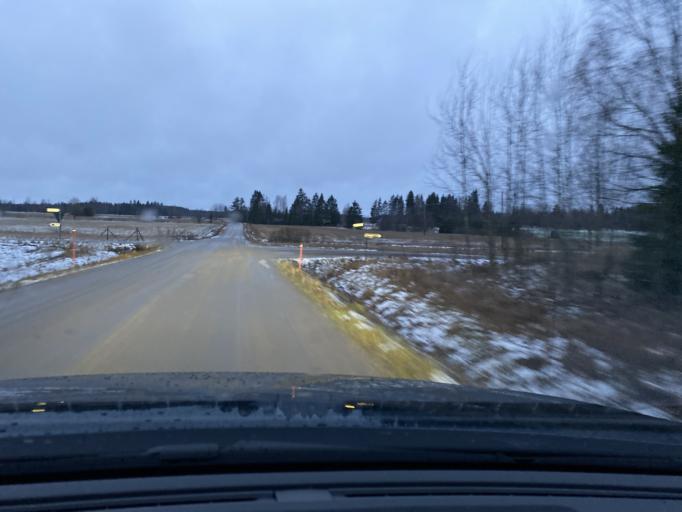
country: FI
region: Pirkanmaa
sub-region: Lounais-Pirkanmaa
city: Punkalaidun
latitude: 61.1191
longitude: 23.0214
